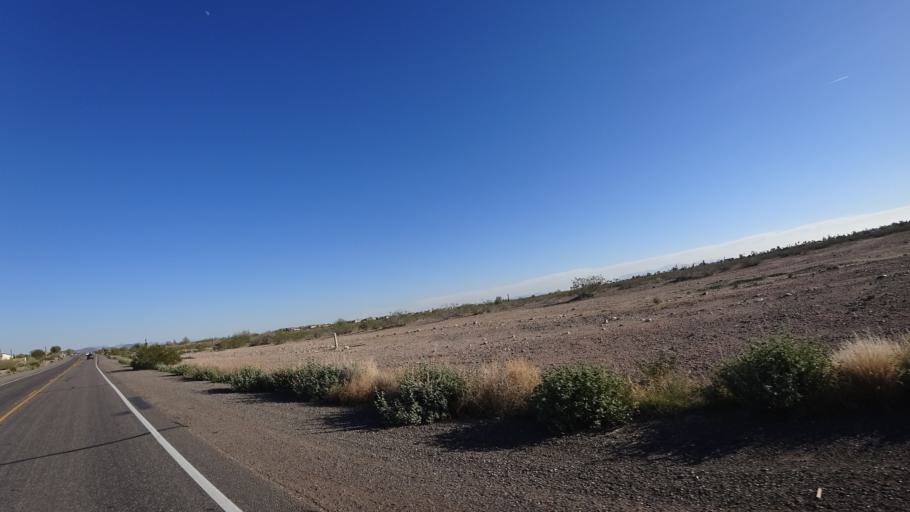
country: US
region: Arizona
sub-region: Maricopa County
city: Sun City West
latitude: 33.6894
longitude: -112.3297
